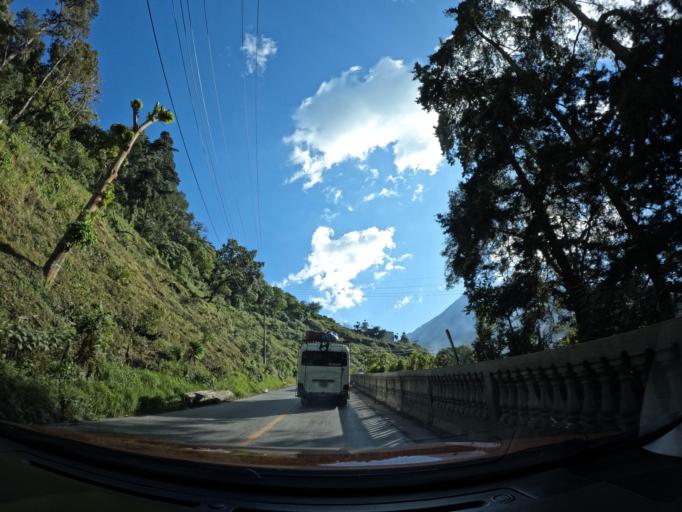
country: GT
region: Sacatepequez
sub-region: Municipio de Santa Maria de Jesus
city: Santa Maria de Jesus
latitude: 14.5002
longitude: -90.7099
